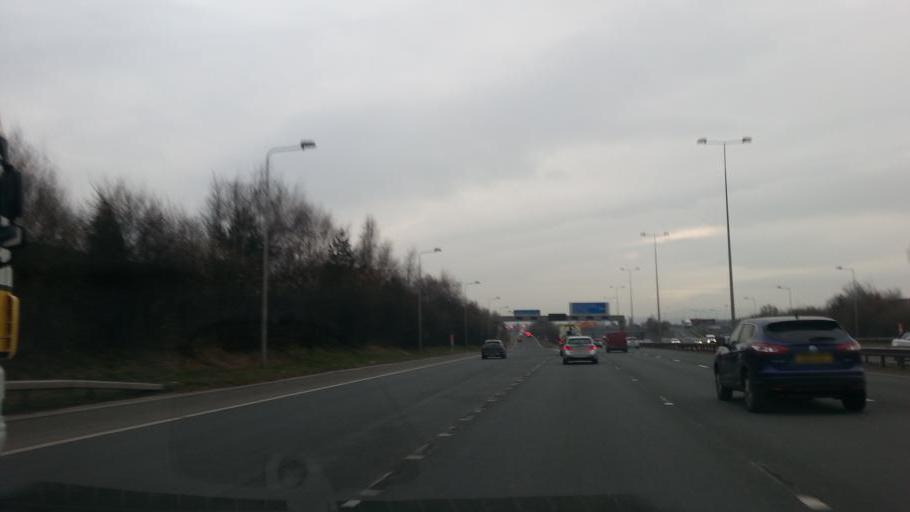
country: GB
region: England
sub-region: Borough of Tameside
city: Denton
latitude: 53.4757
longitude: -2.1256
